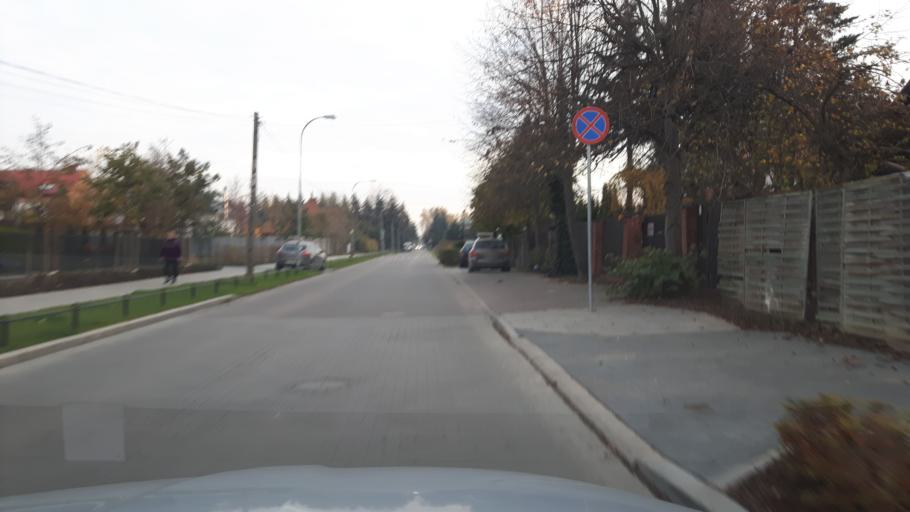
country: PL
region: Masovian Voivodeship
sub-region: Warszawa
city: Wilanow
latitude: 52.1744
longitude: 21.1111
